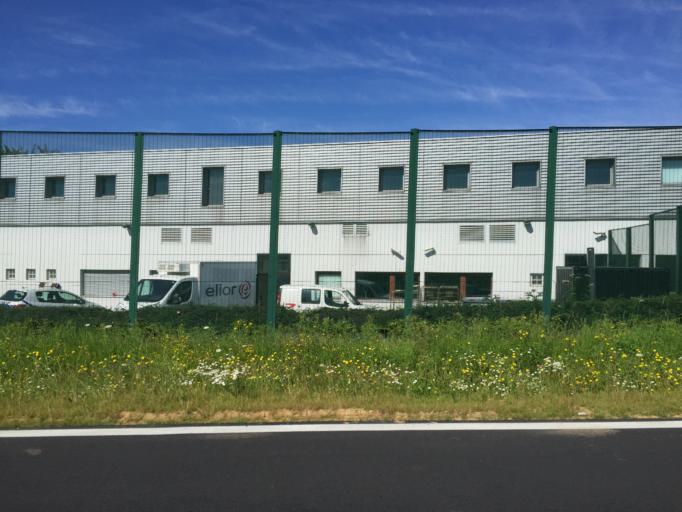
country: FR
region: Ile-de-France
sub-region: Departement du Val-d'Oise
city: Roissy-en-France
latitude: 49.0055
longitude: 2.5518
